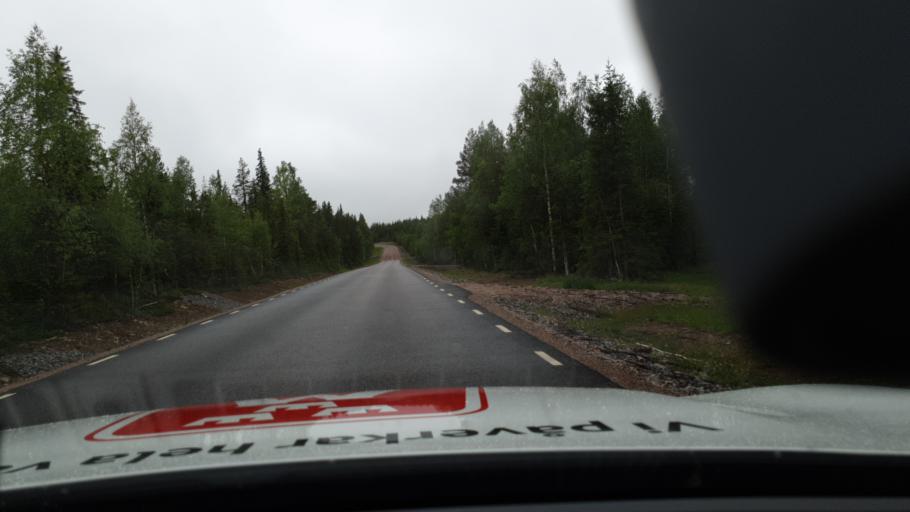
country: SE
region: Norrbotten
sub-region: Overtornea Kommun
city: OEvertornea
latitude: 66.5032
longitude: 23.4191
